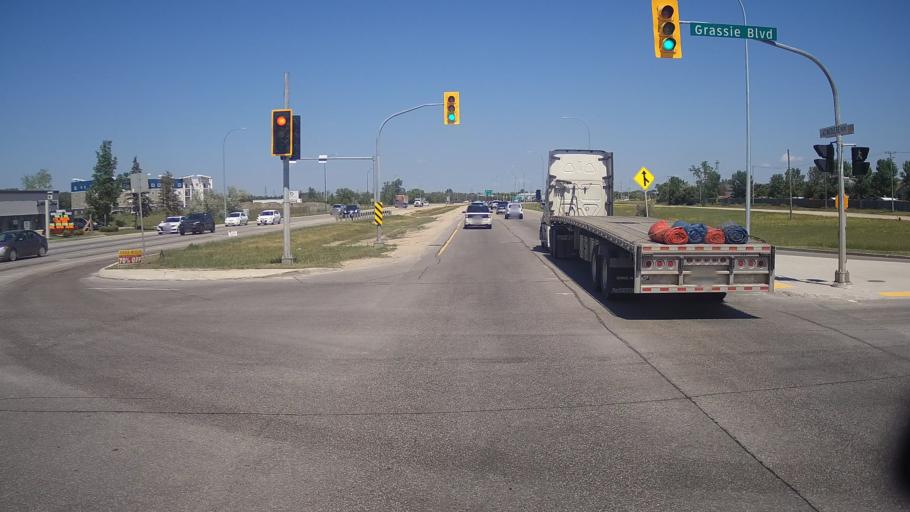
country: CA
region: Manitoba
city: Winnipeg
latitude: 49.9224
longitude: -97.0482
